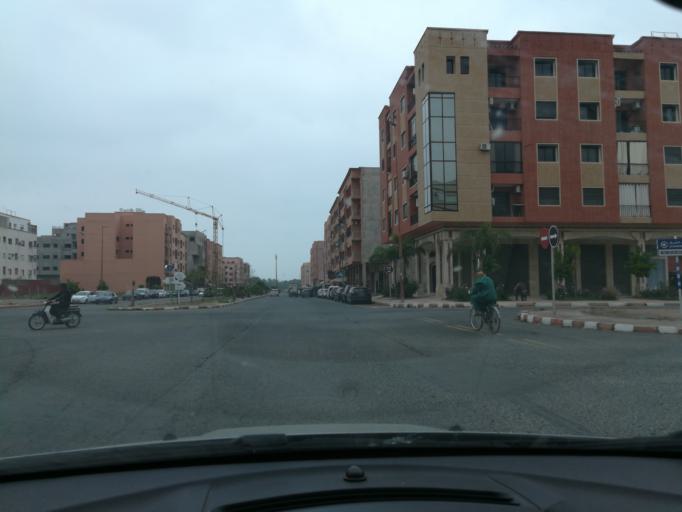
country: MA
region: Marrakech-Tensift-Al Haouz
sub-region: Marrakech
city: Marrakesh
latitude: 31.6749
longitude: -8.0267
